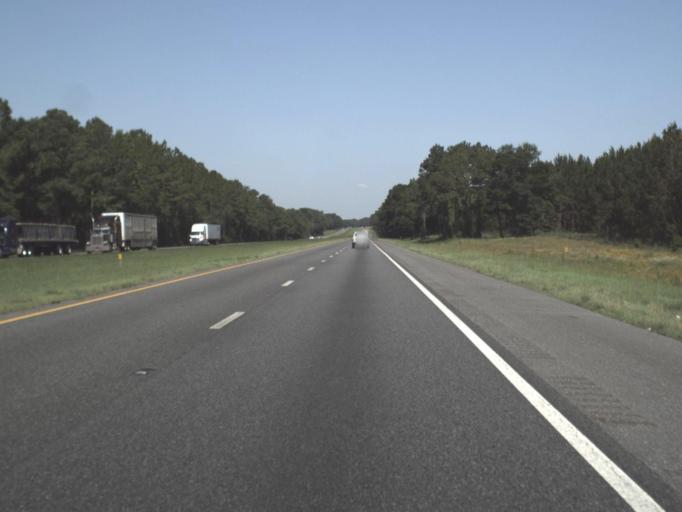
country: US
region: Florida
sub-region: Suwannee County
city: Wellborn
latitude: 30.2892
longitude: -82.8603
